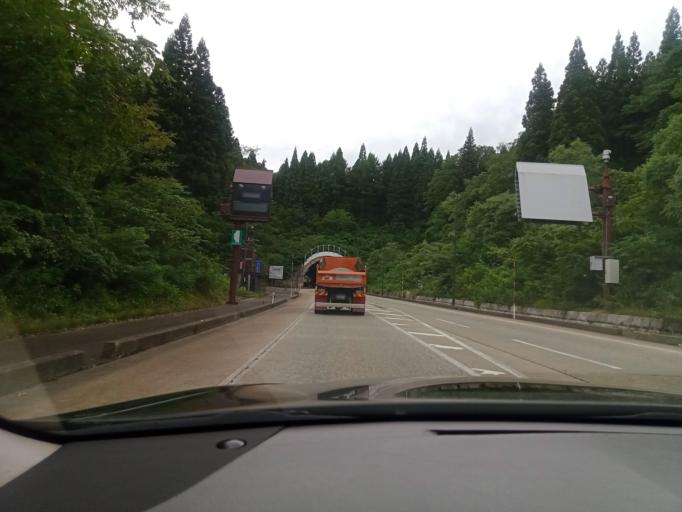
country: JP
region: Niigata
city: Arai
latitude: 36.8740
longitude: 138.2013
